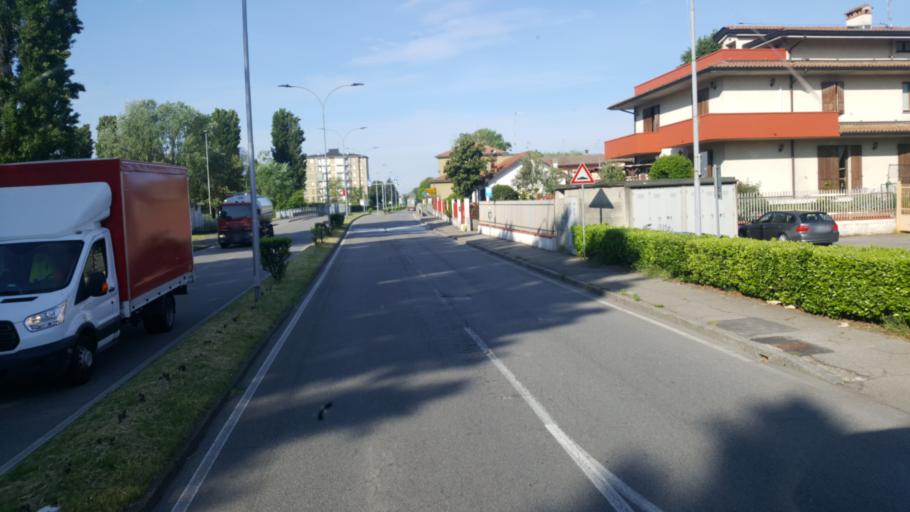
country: IT
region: Lombardy
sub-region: Citta metropolitana di Milano
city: Melzo
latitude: 45.4967
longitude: 9.4174
